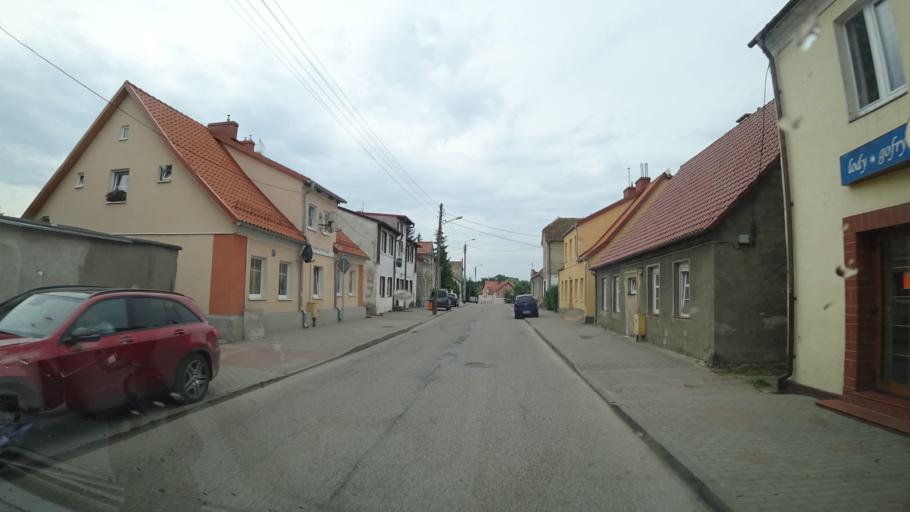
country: PL
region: Warmian-Masurian Voivodeship
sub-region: Powiat gizycki
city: Ryn
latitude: 53.9367
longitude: 21.5474
